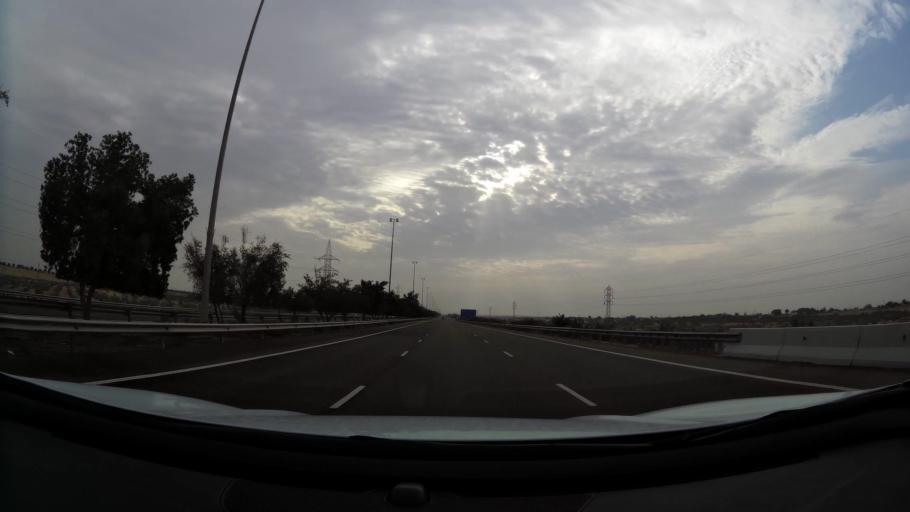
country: AE
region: Abu Dhabi
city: Abu Dhabi
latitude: 24.2032
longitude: 54.9032
